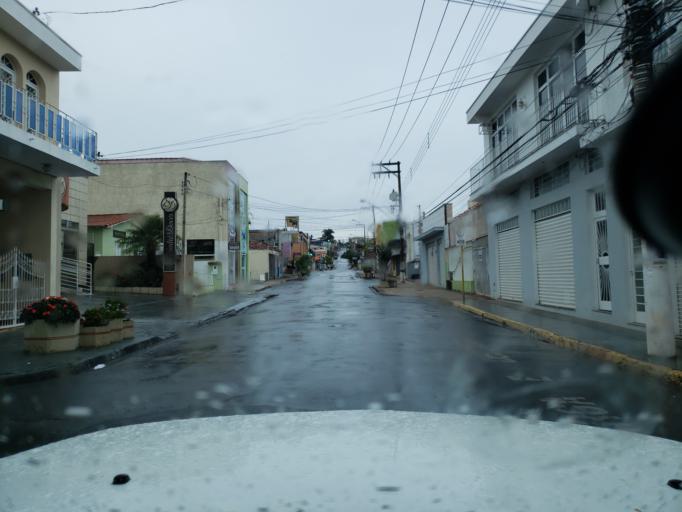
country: BR
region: Sao Paulo
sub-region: Moji-Guacu
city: Mogi-Gaucu
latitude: -22.3678
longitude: -46.9429
